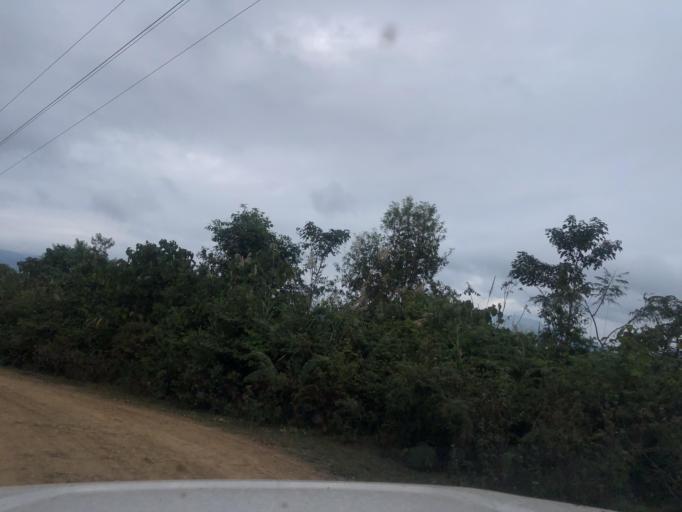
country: LA
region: Phongsali
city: Khoa
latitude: 21.2658
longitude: 102.5894
